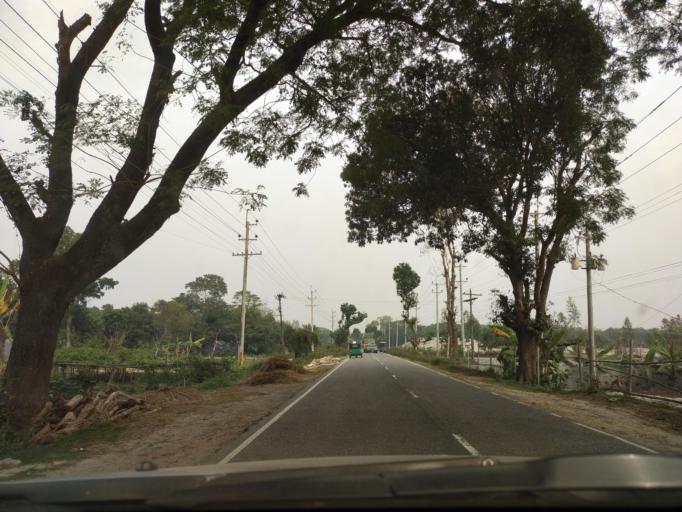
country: BD
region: Dhaka
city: Narsingdi
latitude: 24.0094
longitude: 90.7373
